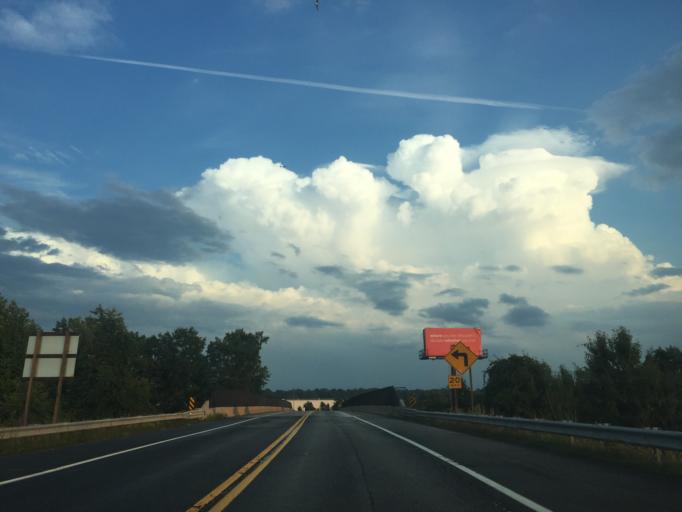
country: US
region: Maryland
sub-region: Harford County
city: Riverside
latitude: 39.4721
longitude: -76.2353
